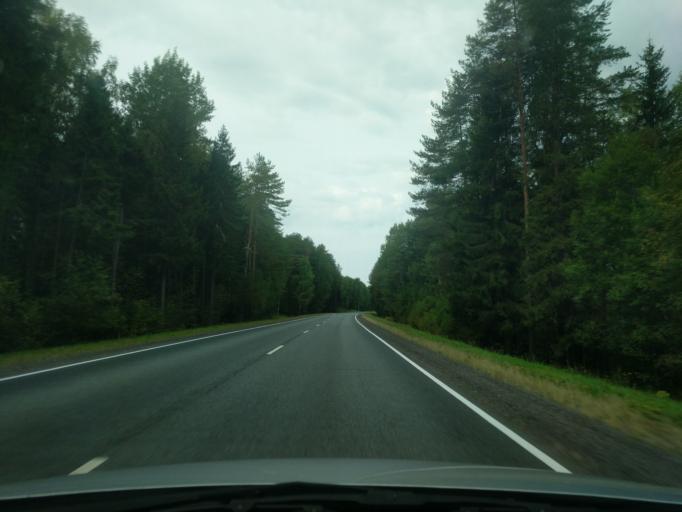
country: RU
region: Kirov
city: Svecha
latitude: 58.2708
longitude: 47.7233
